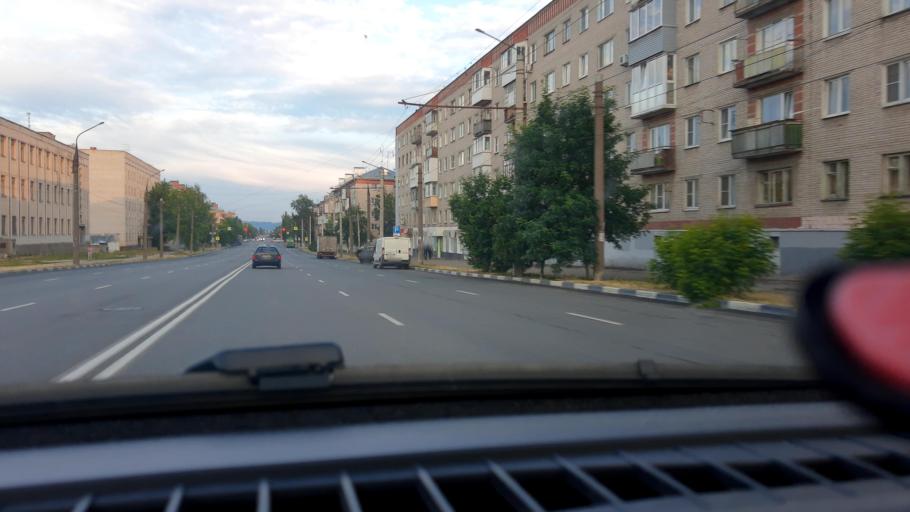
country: RU
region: Nizjnij Novgorod
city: Dzerzhinsk
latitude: 56.2437
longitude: 43.4792
